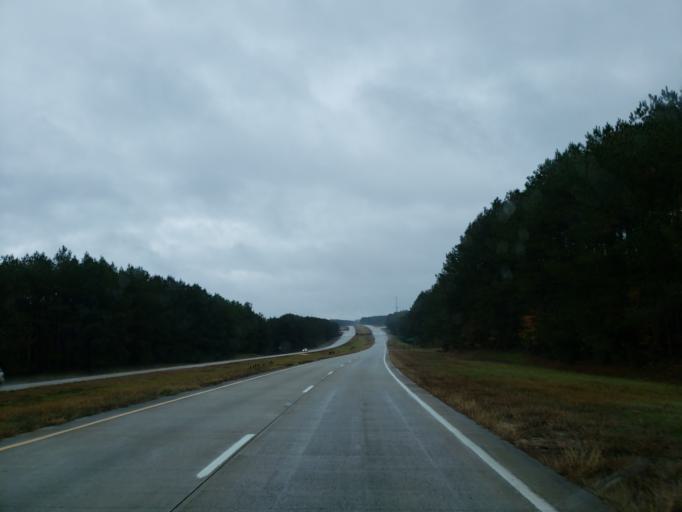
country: US
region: Mississippi
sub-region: Lauderdale County
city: Meridian
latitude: 32.3275
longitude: -88.6717
